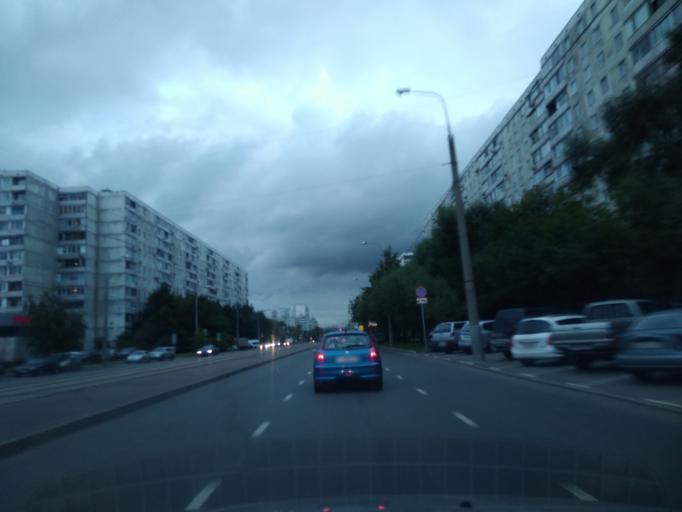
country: RU
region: Moscow
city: Strogino
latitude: 55.8084
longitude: 37.3962
